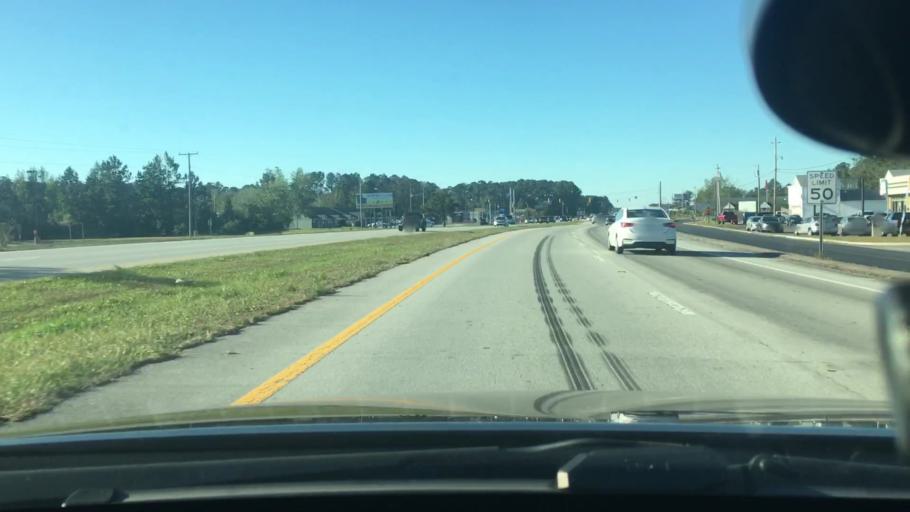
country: US
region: North Carolina
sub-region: Craven County
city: Havelock
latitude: 34.8945
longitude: -76.9259
